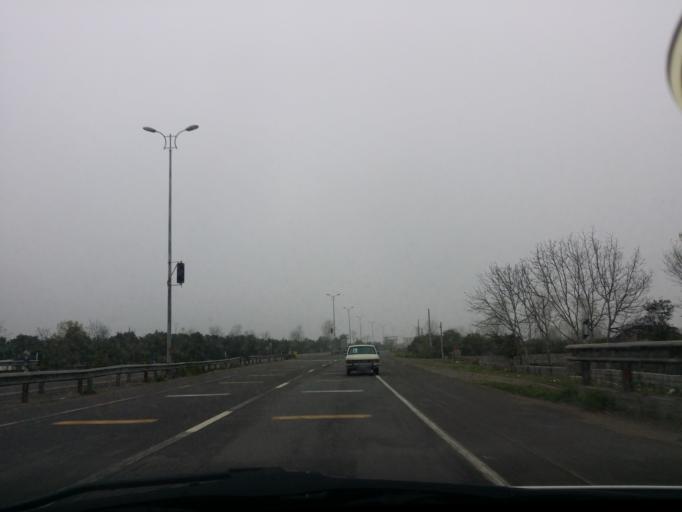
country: IR
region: Mazandaran
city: Tonekabon
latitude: 36.8179
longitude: 50.8499
